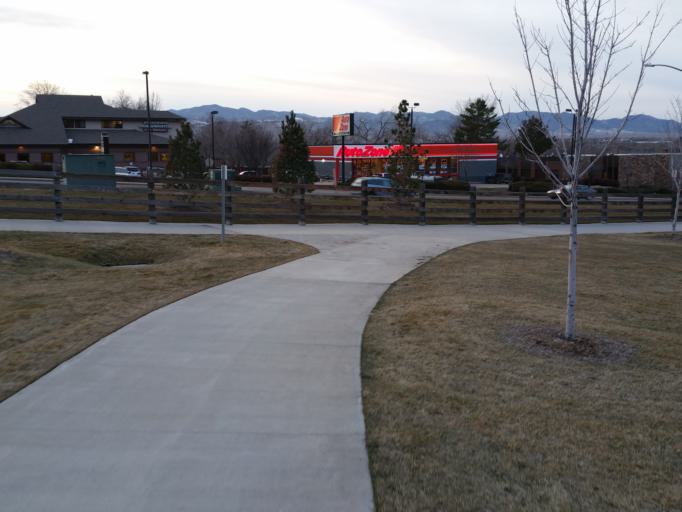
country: US
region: Colorado
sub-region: Jefferson County
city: Wheat Ridge
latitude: 39.7666
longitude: -105.1091
